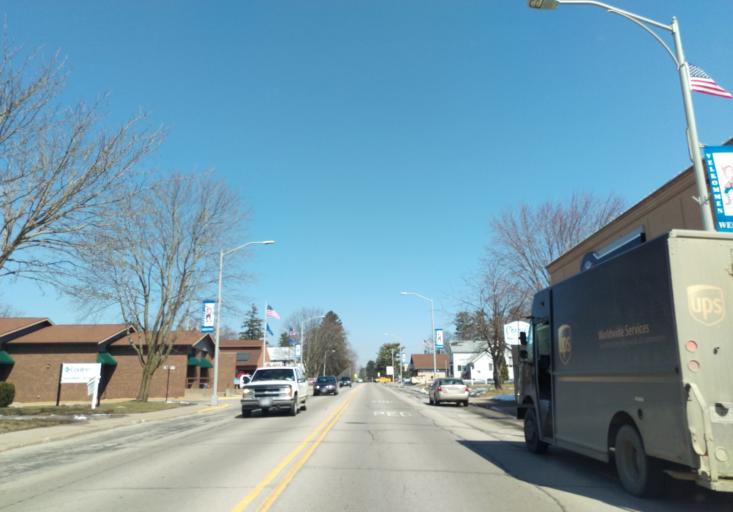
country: US
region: Wisconsin
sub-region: Vernon County
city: Westby
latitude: 43.6539
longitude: -90.8570
